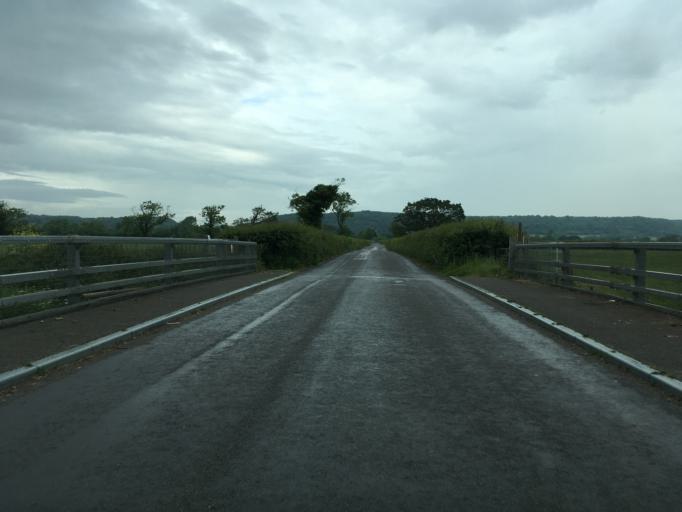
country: GB
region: England
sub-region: North Somerset
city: Kenn
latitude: 51.4245
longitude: -2.8320
